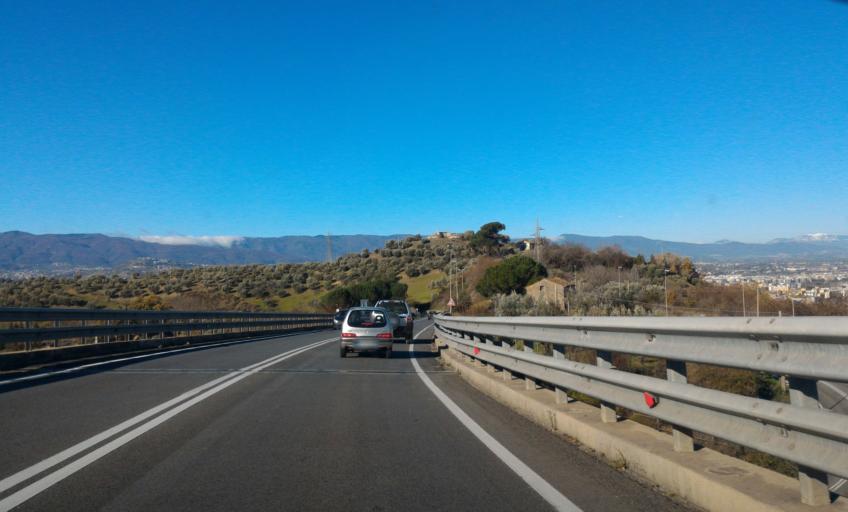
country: IT
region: Calabria
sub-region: Provincia di Cosenza
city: Cosenza
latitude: 39.2948
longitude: 16.2718
